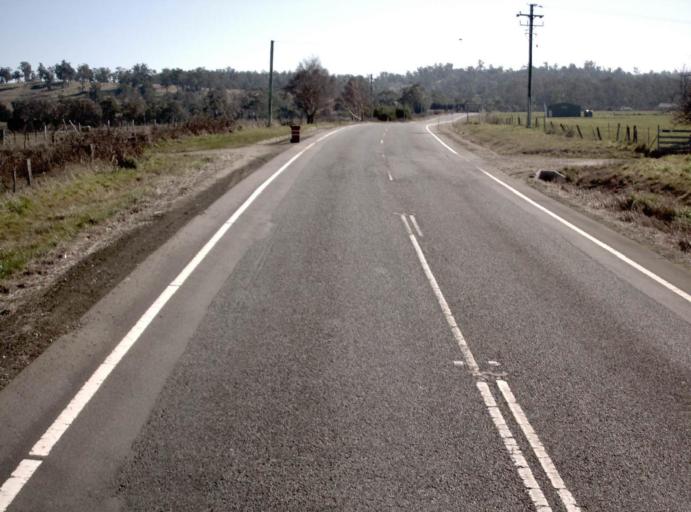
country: AU
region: Tasmania
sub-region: Launceston
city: Mayfield
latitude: -41.3158
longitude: 147.0545
